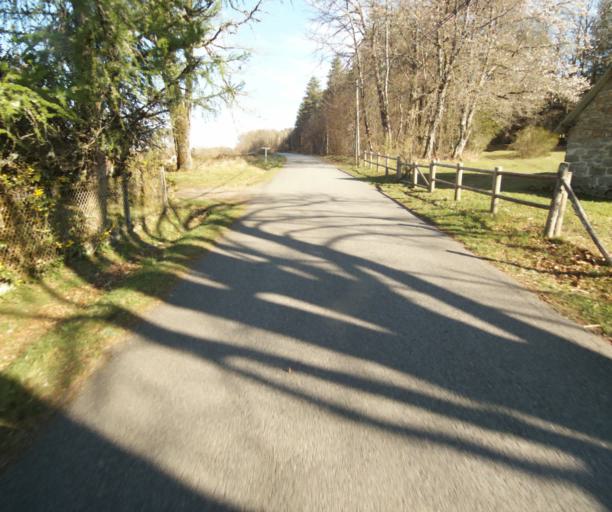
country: FR
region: Limousin
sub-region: Departement de la Correze
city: Correze
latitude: 45.3244
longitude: 1.8846
